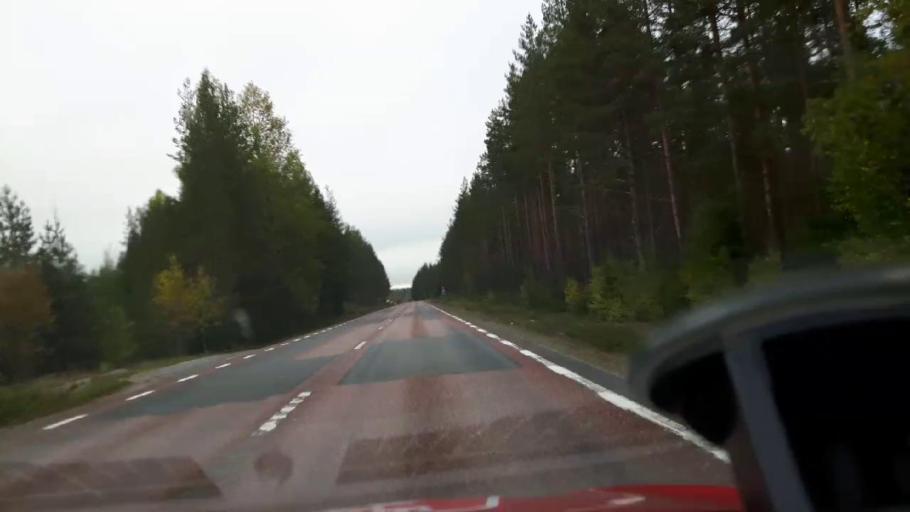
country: SE
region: Gaevleborg
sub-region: Ljusdals Kommun
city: Farila
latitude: 61.8464
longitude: 15.7513
